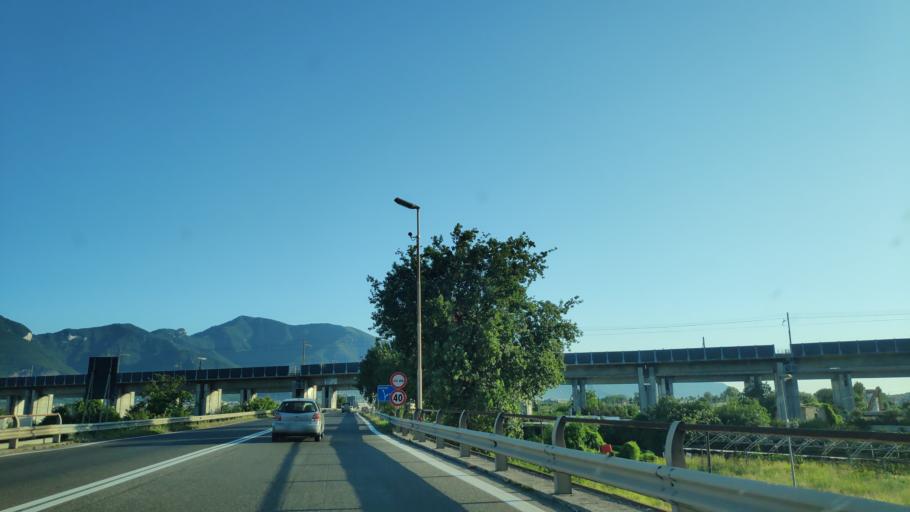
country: IT
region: Campania
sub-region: Provincia di Salerno
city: San Valentino Torio
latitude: 40.7779
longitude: 14.6161
